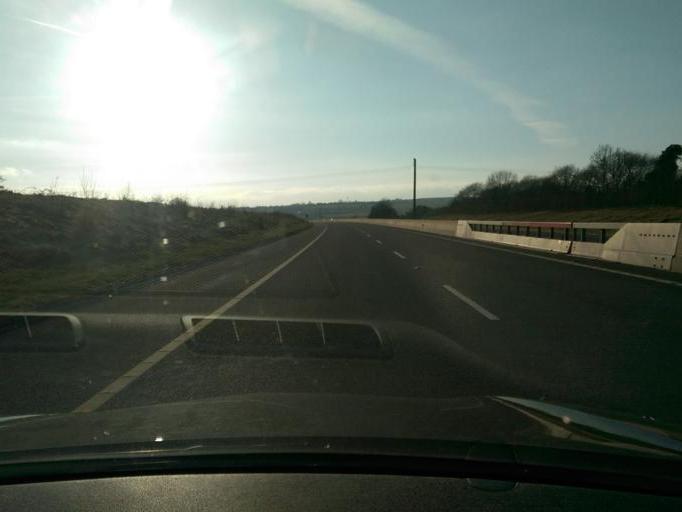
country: IE
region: Munster
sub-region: North Tipperary
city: Roscrea
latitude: 52.9271
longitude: -7.7653
